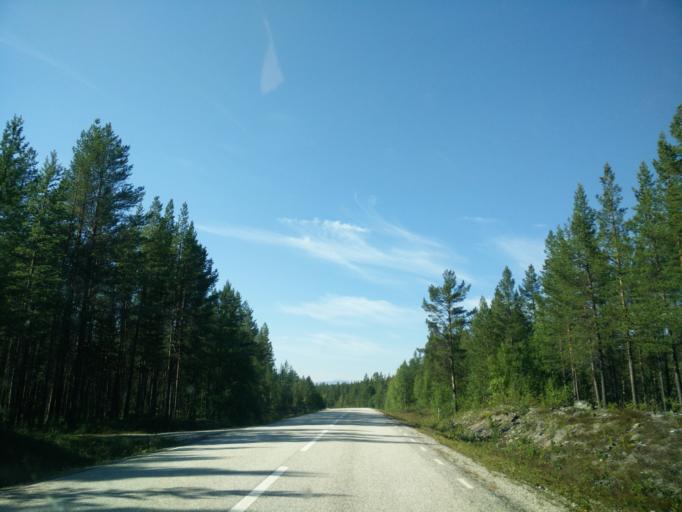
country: SE
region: Jaemtland
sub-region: Are Kommun
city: Jarpen
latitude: 62.8277
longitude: 13.4646
